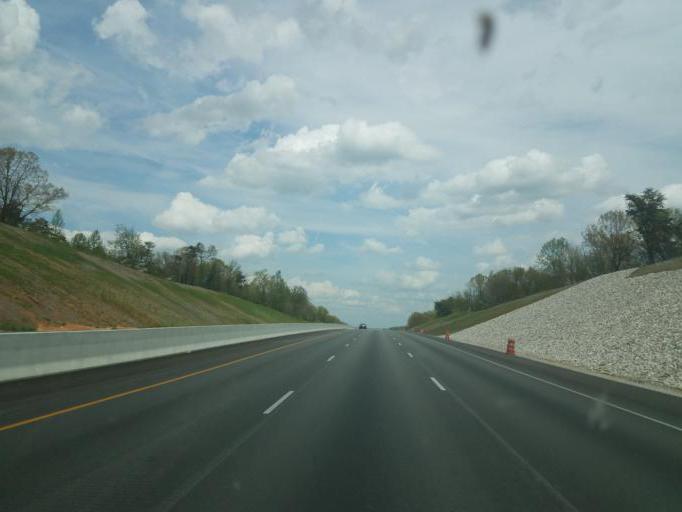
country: US
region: Kentucky
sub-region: Hart County
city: Munfordville
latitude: 37.3224
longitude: -85.9059
